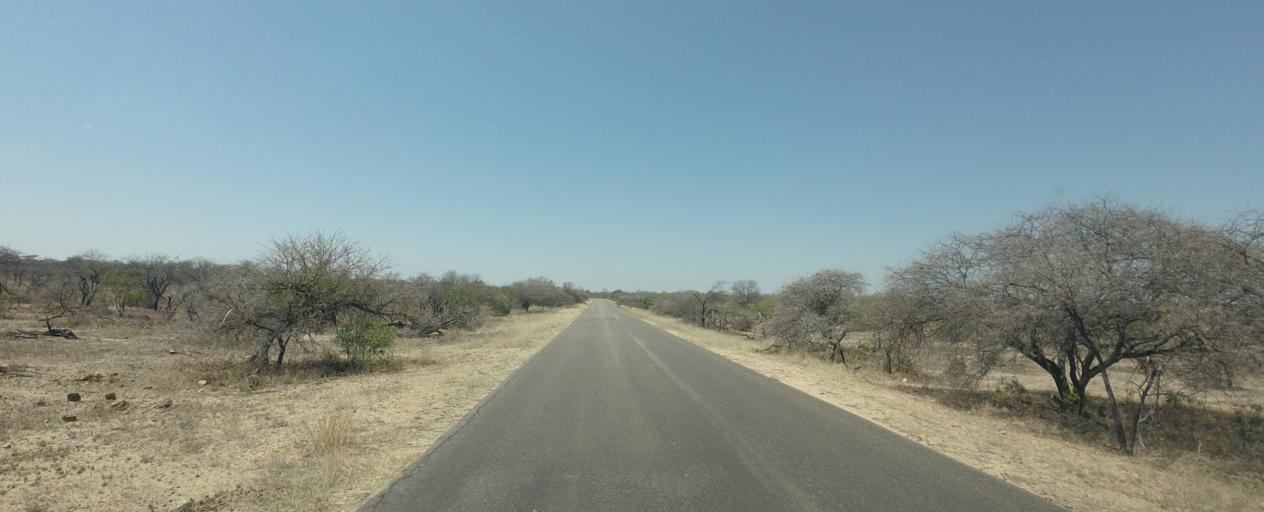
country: ZA
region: Limpopo
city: Thulamahashi
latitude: -24.4364
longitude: 31.4936
